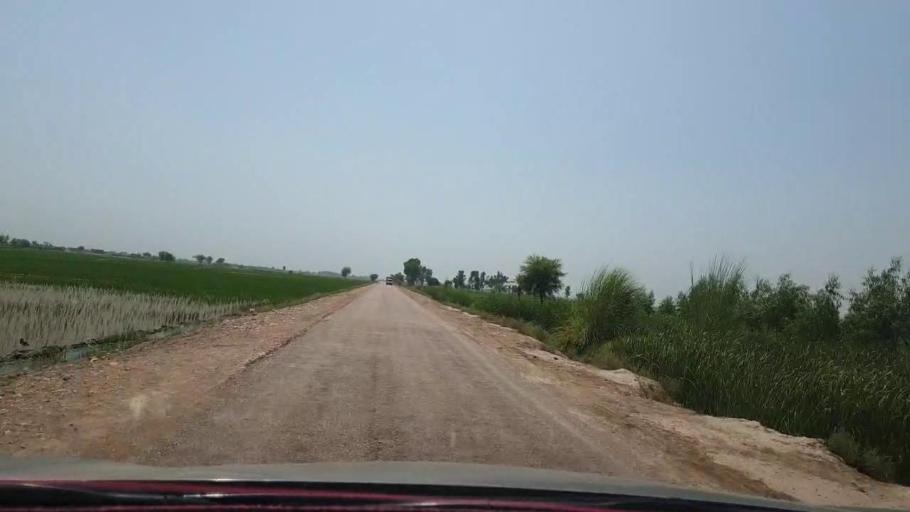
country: PK
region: Sindh
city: Warah
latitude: 27.5624
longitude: 67.8009
